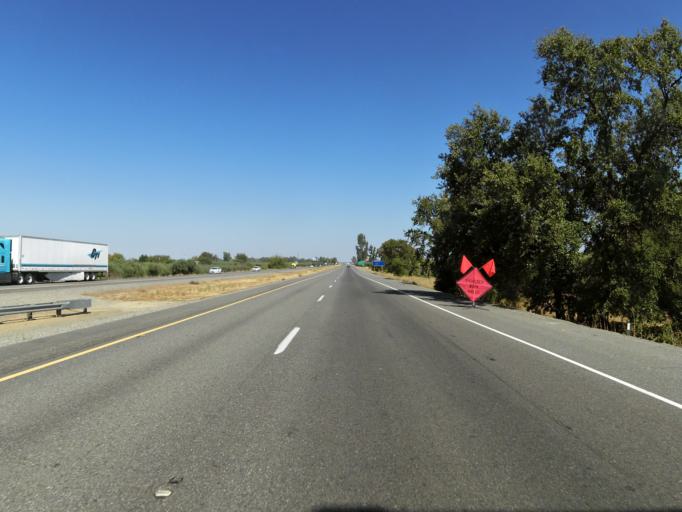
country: US
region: California
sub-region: Tehama County
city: Corning
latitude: 39.8853
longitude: -122.2000
